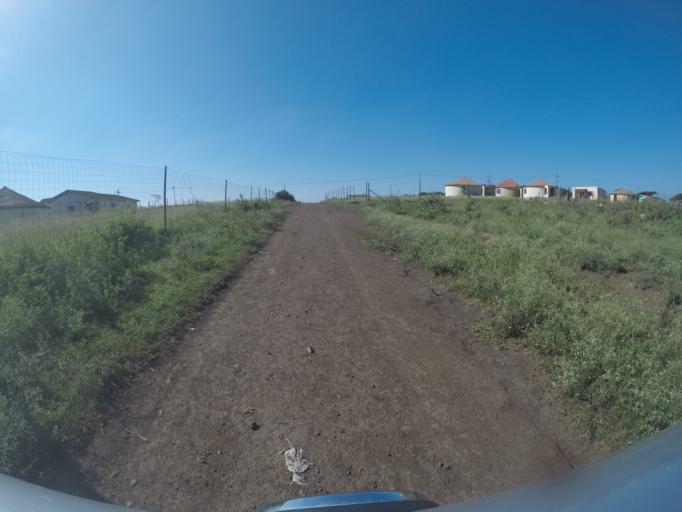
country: ZA
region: KwaZulu-Natal
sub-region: uThungulu District Municipality
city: Empangeni
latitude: -28.5724
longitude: 31.7306
